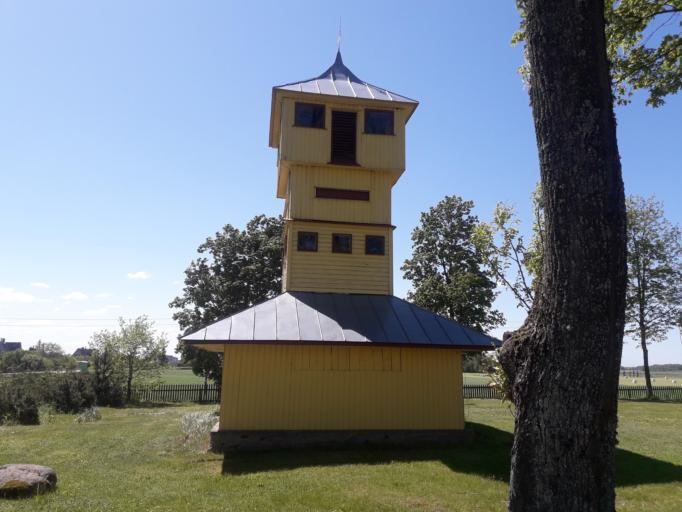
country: LT
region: Kauno apskritis
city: Dainava (Kaunas)
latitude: 54.7900
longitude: 24.0514
